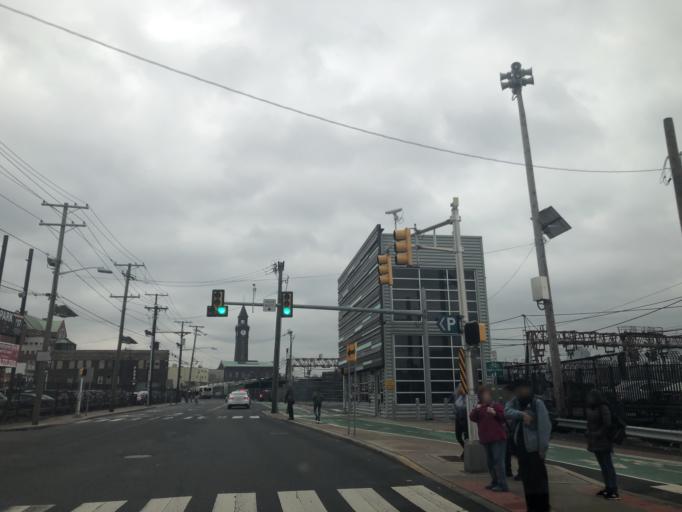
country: US
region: New Jersey
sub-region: Hudson County
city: Hoboken
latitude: 40.7331
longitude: -74.0324
